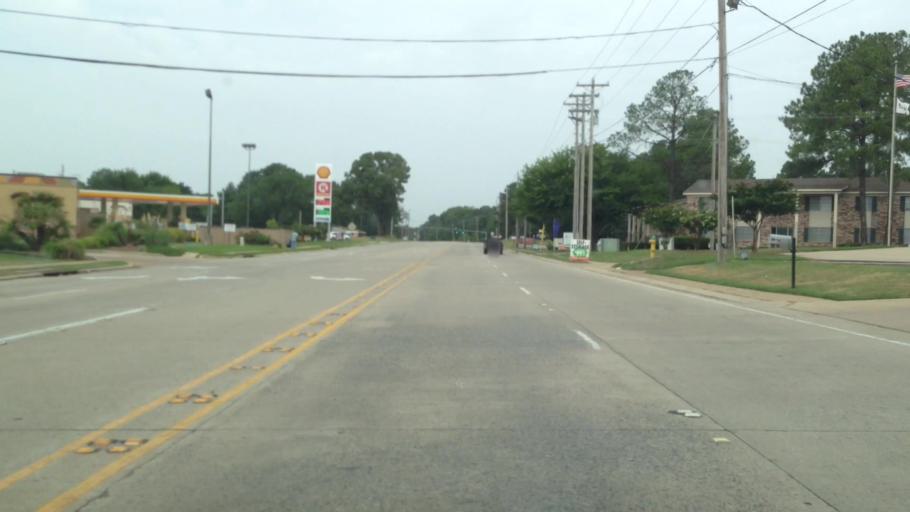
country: US
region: Louisiana
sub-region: De Soto Parish
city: Stonewall
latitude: 32.3960
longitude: -93.8109
